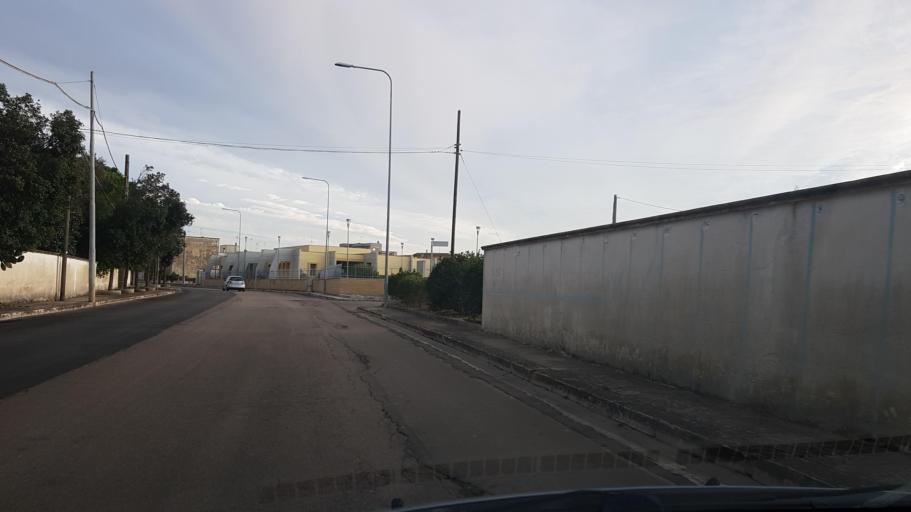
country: IT
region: Apulia
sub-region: Provincia di Lecce
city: Surbo
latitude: 40.4011
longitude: 18.1279
